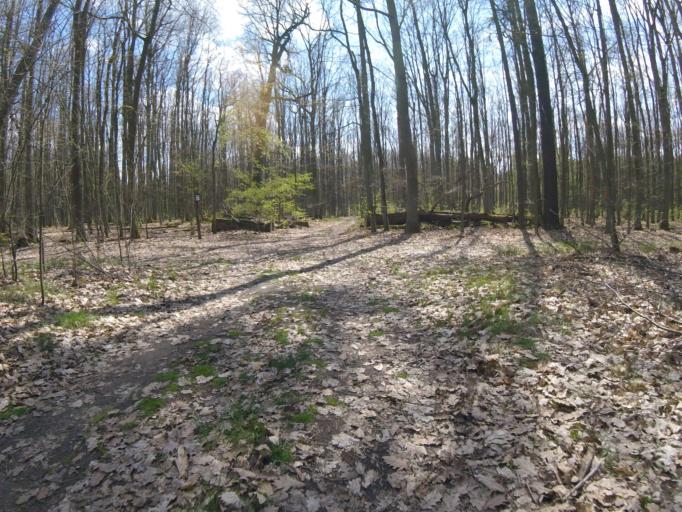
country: DE
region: Brandenburg
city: Gross Koris
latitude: 52.2060
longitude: 13.7226
